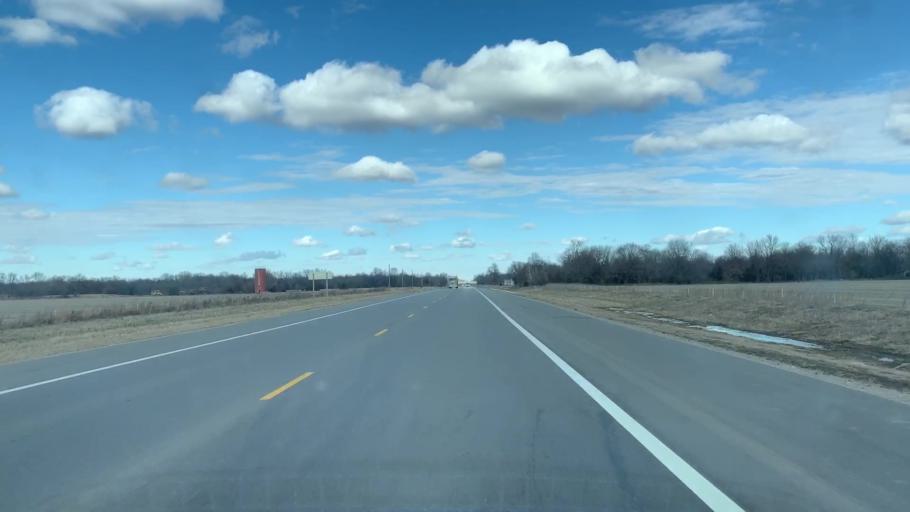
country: US
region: Kansas
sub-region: Cherokee County
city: Columbus
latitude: 37.2672
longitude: -94.8321
